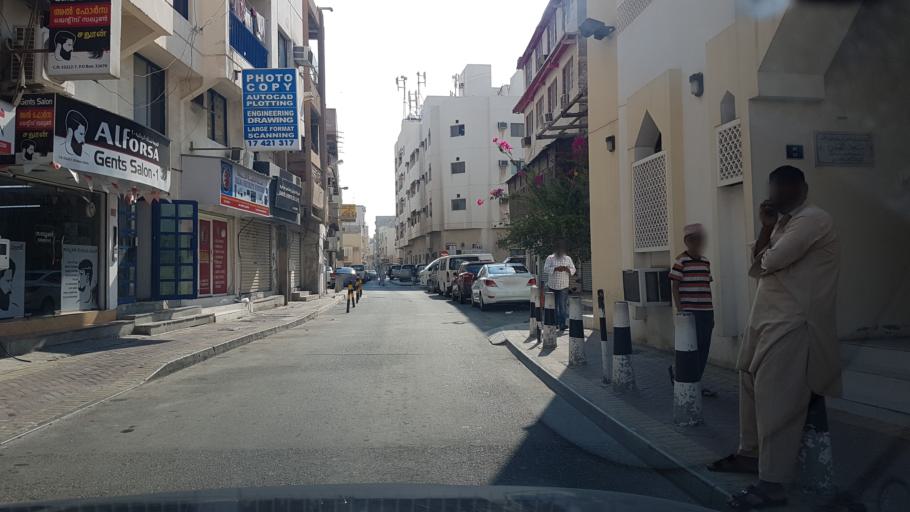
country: BH
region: Manama
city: Manama
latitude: 26.2346
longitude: 50.5799
